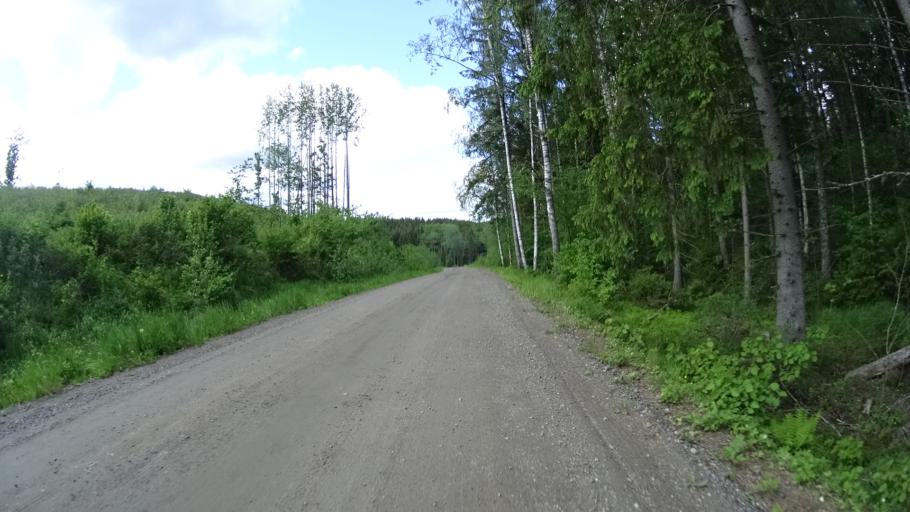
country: FI
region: Uusimaa
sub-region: Raaseporin
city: Pohja
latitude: 60.1609
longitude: 23.6062
